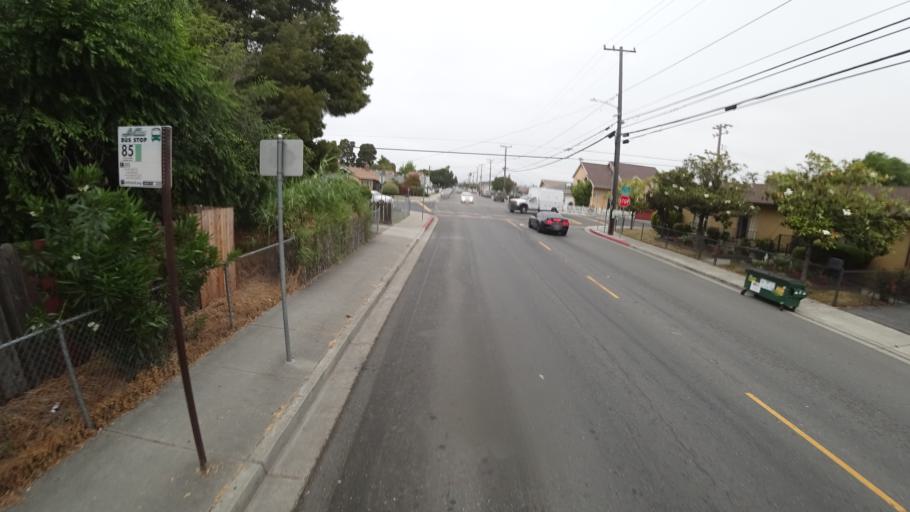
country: US
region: California
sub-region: Alameda County
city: Hayward
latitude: 37.6250
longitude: -122.0659
